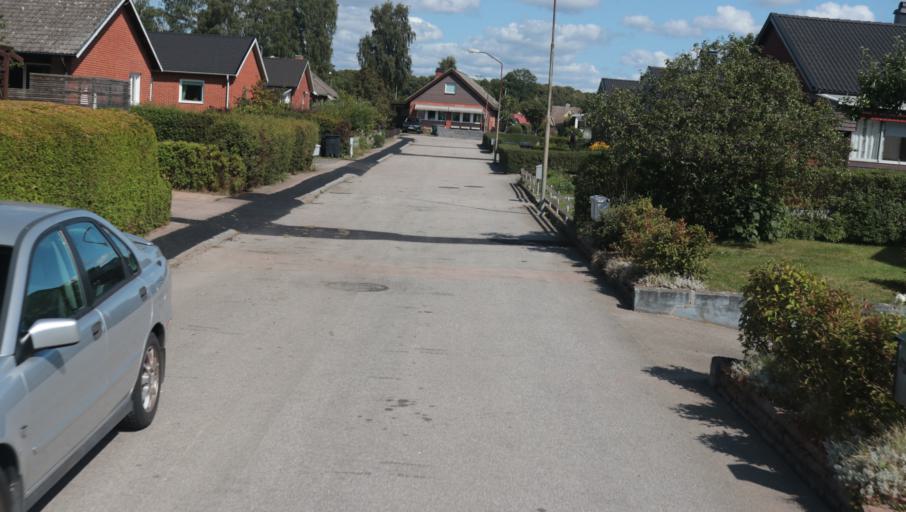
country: SE
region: Blekinge
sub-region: Karlshamns Kommun
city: Karlshamn
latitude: 56.1998
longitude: 14.8279
